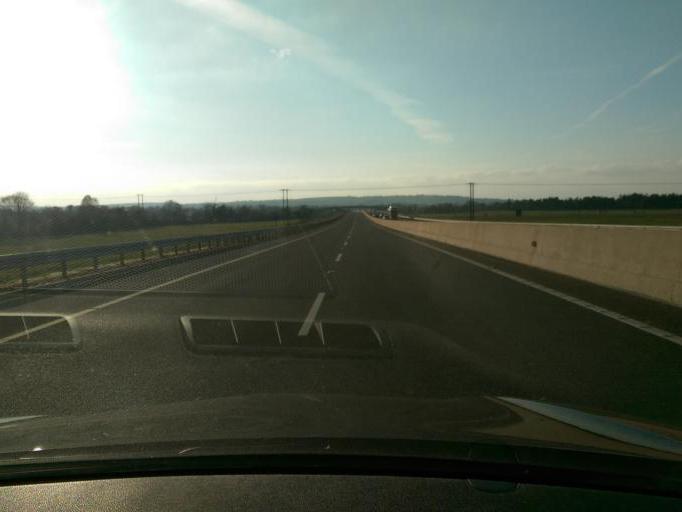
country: IE
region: Munster
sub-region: North Tipperary
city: Roscrea
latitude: 52.9242
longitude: -7.7372
